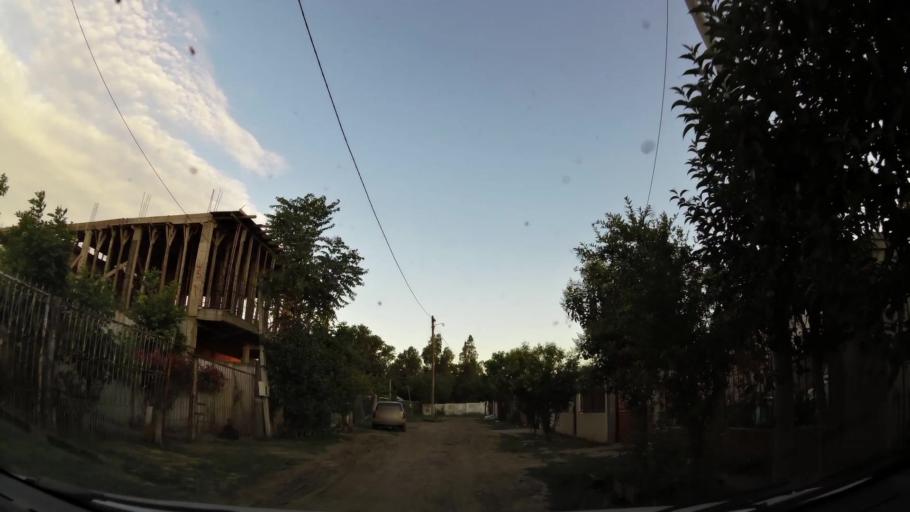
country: AR
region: Buenos Aires
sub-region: Partido de Merlo
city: Merlo
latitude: -34.6734
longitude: -58.7813
